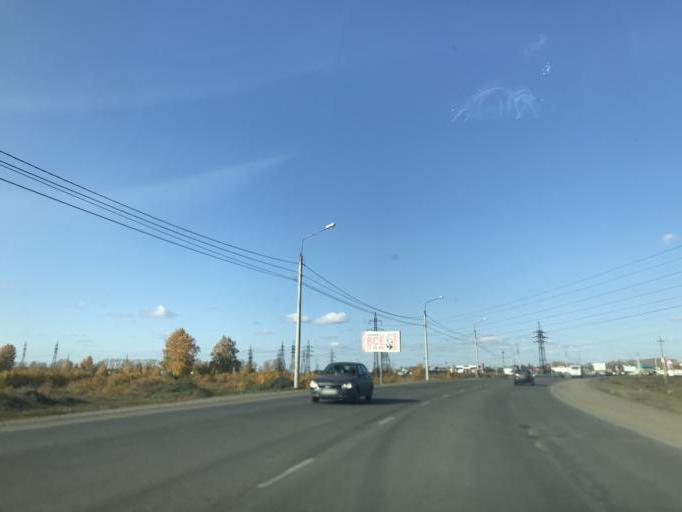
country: RU
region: Chelyabinsk
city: Roshchino
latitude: 55.2268
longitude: 61.2875
